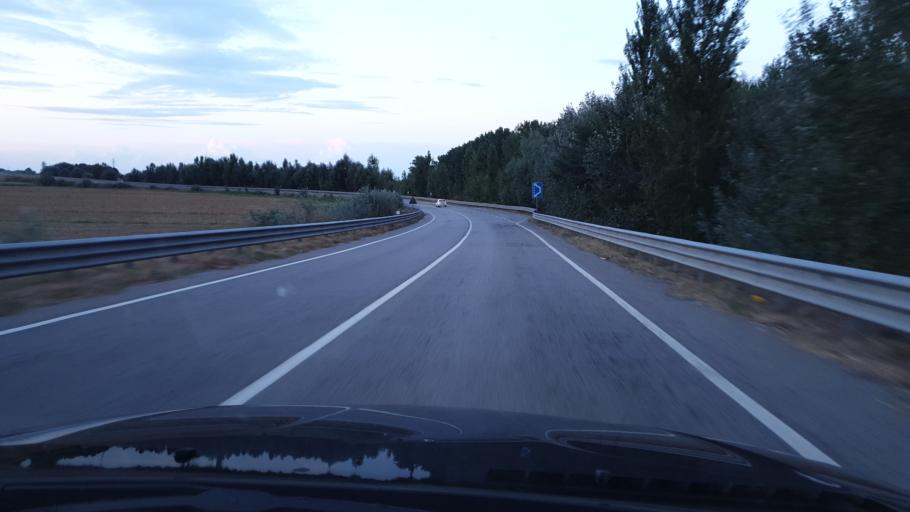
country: IT
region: Emilia-Romagna
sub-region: Provincia di Ravenna
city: Alfonsine
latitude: 44.5004
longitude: 12.0606
